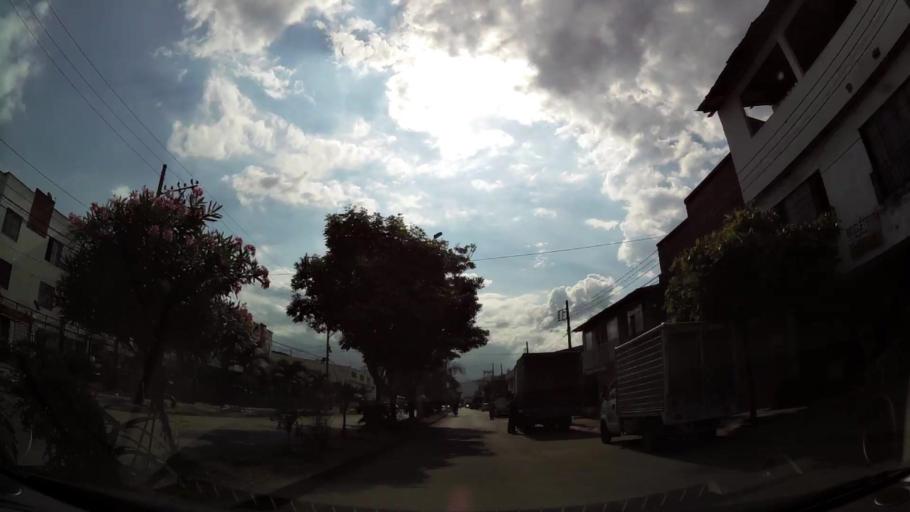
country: CO
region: Valle del Cauca
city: Cali
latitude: 3.4705
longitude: -76.5067
